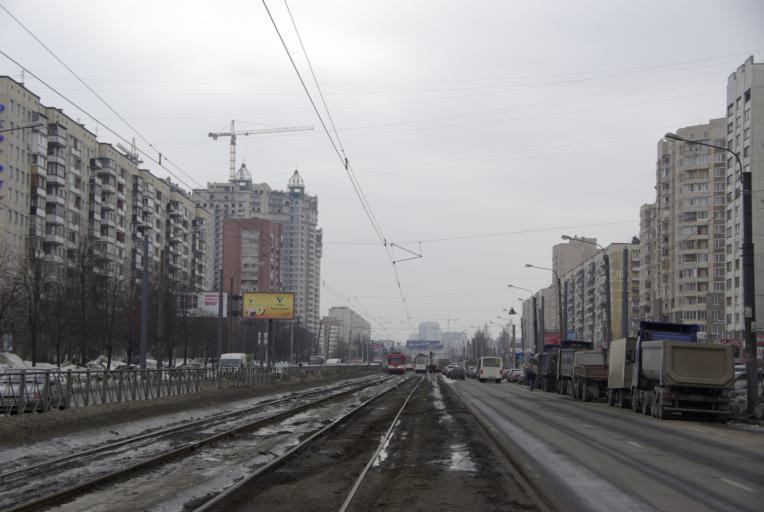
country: RU
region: St.-Petersburg
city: Ozerki
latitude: 60.0496
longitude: 30.3326
